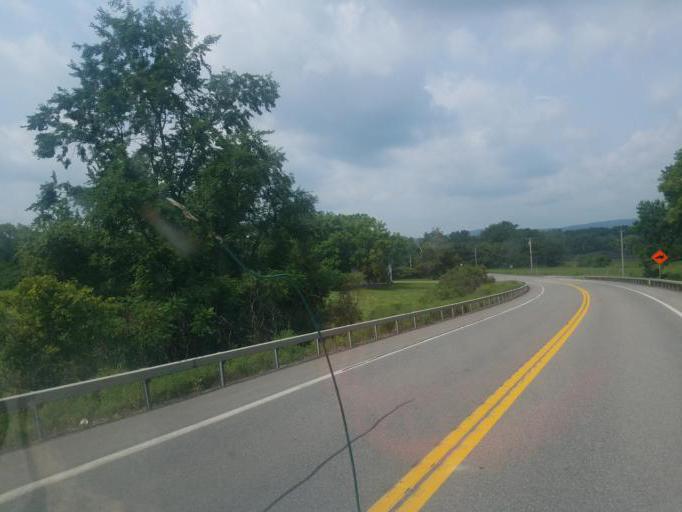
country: US
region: New York
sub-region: Herkimer County
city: Herkimer
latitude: 43.0159
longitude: -74.9492
